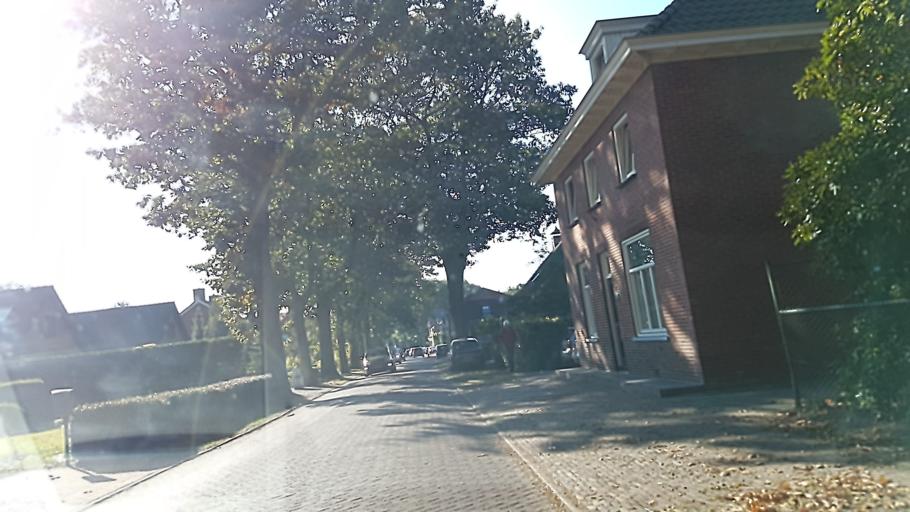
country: NL
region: North Brabant
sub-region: Gemeente Woensdrecht
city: Woensdrecht
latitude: 51.4335
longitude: 4.3824
